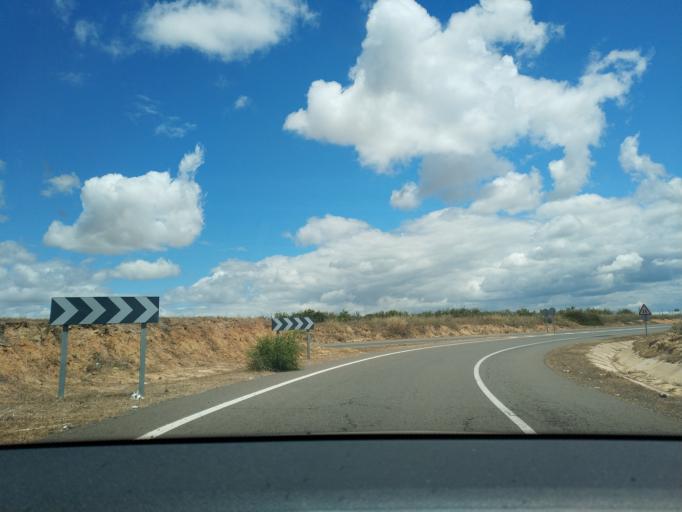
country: ES
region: Andalusia
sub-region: Provincia de Huelva
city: Aljaraque
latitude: 37.3243
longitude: -7.0749
